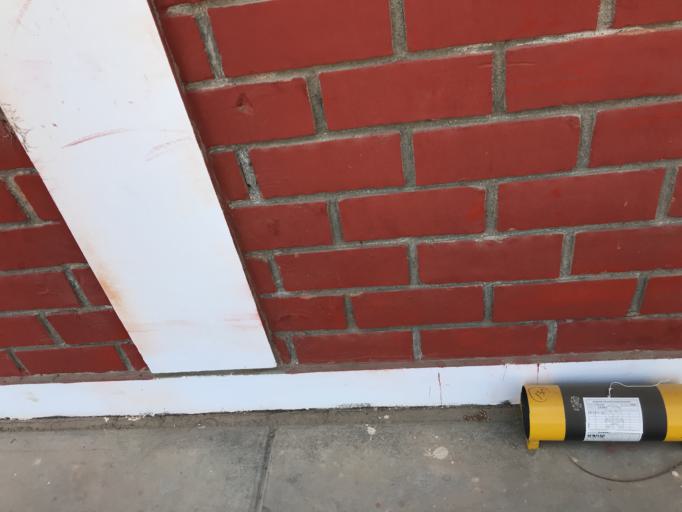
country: PE
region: Ica
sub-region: Provincia de Ica
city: Subtanjalla
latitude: -13.9979
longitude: -75.7701
